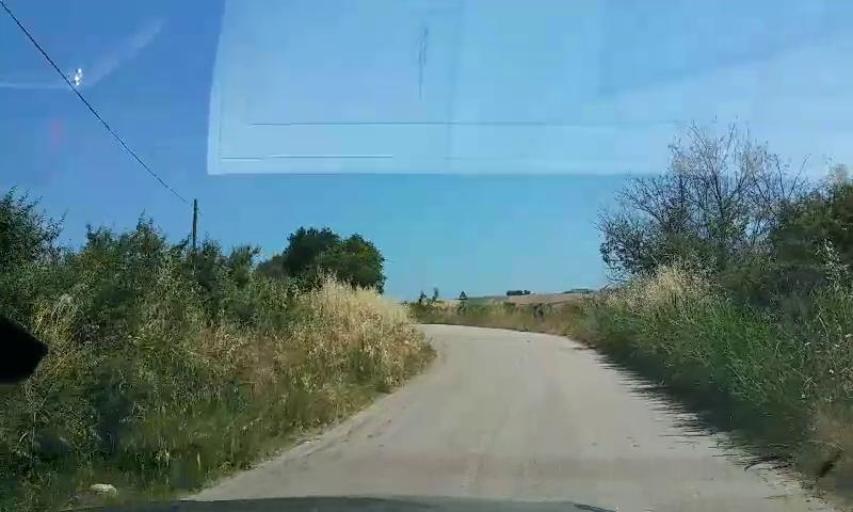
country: IT
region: Molise
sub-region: Provincia di Campobasso
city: Guglionesi
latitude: 41.9433
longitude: 14.8977
